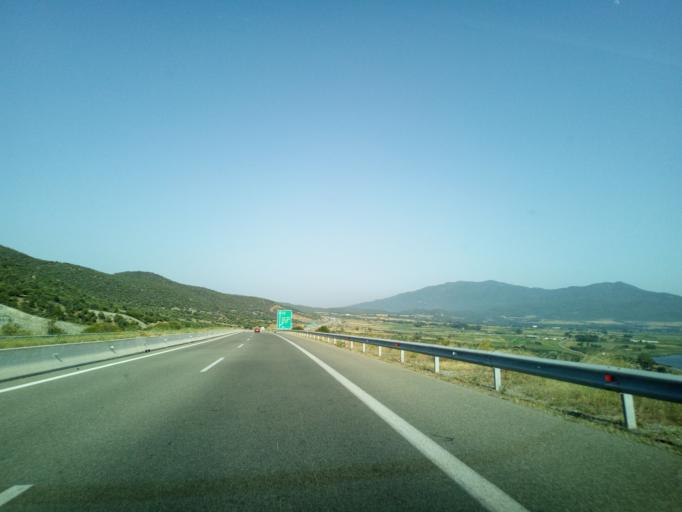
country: GR
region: Central Macedonia
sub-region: Nomos Thessalonikis
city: Stavros
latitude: 40.6803
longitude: 23.5700
